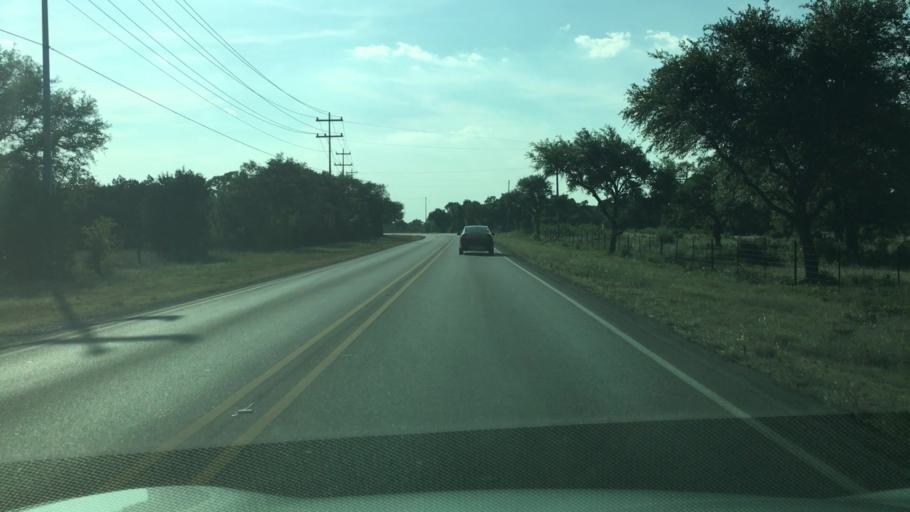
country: US
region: Texas
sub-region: Travis County
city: Shady Hollow
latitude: 30.1160
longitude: -97.9544
